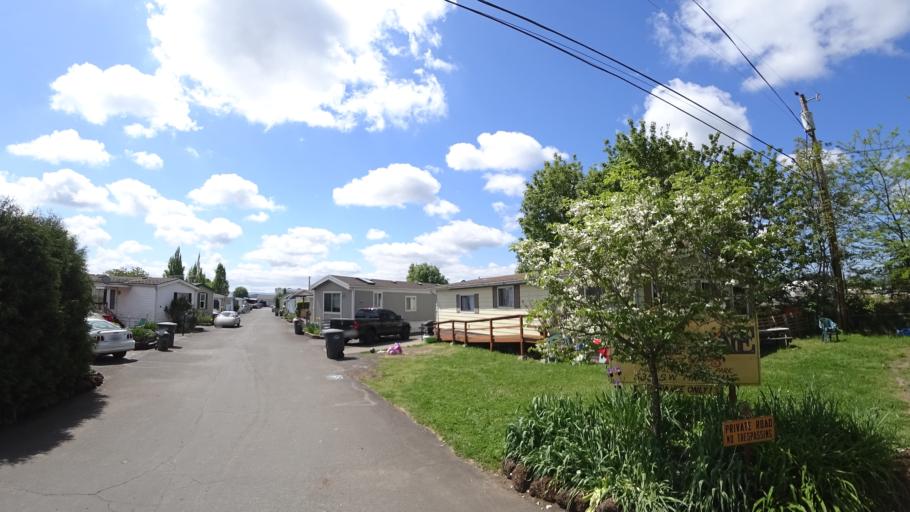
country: US
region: Oregon
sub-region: Washington County
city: Hillsboro
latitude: 45.5163
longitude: -122.9967
